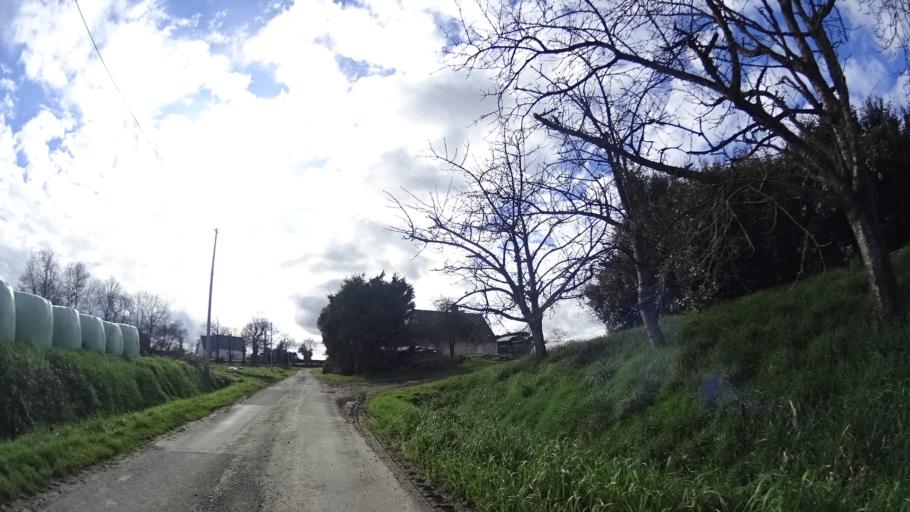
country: FR
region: Brittany
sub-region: Departement des Cotes-d'Armor
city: Evran
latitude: 48.3264
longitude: -1.9508
